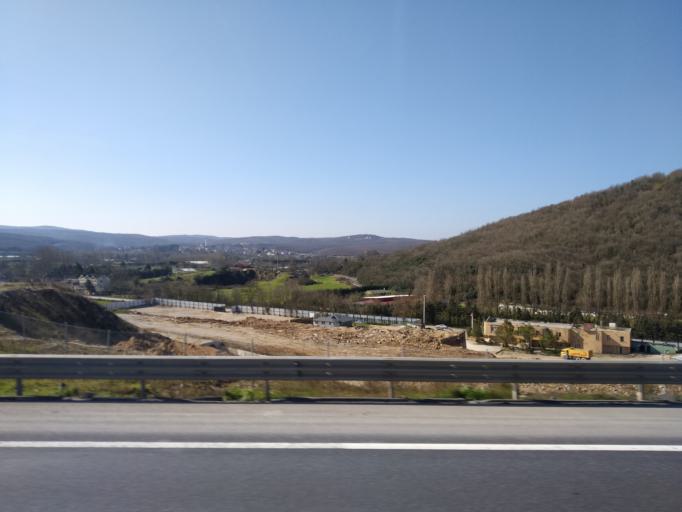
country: TR
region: Istanbul
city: Mahmut Sevket Pasa
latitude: 41.1344
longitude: 29.2868
